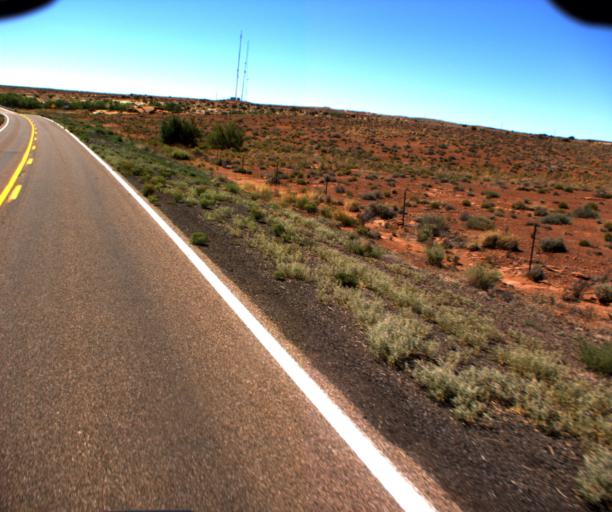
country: US
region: Arizona
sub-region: Navajo County
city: Winslow
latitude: 34.9779
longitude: -110.6564
